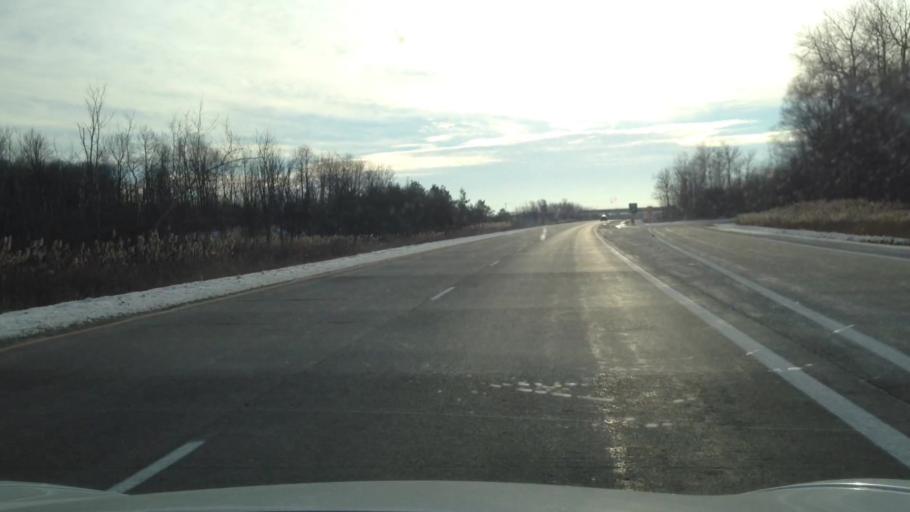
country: CA
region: Ontario
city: Hawkesbury
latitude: 45.4387
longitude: -74.7381
